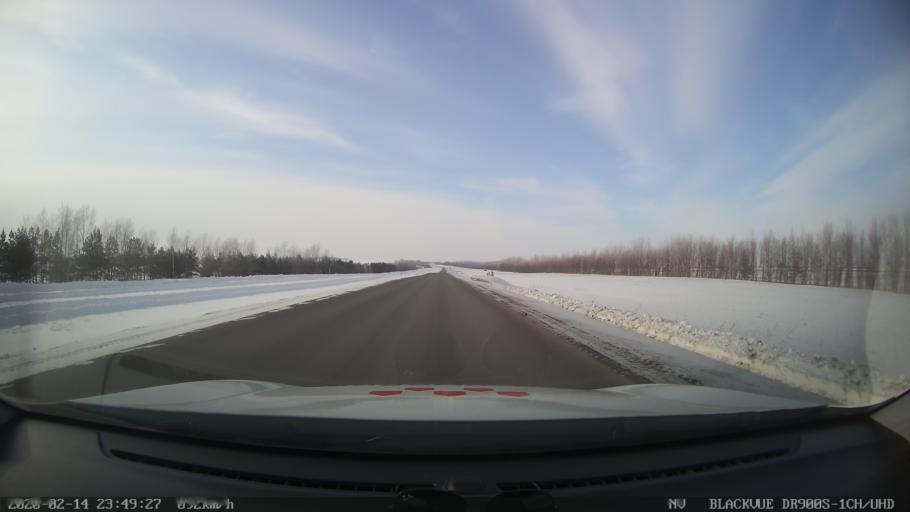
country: RU
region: Tatarstan
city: Kuybyshevskiy Zaton
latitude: 55.2538
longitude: 49.1815
